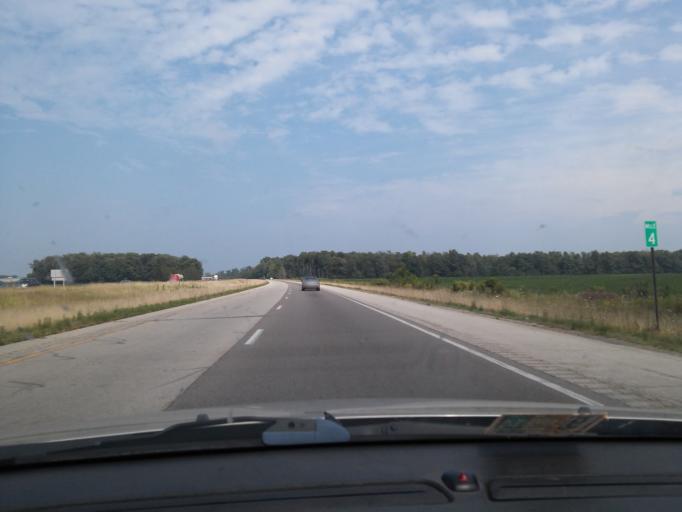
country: US
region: Ohio
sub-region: Preble County
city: New Paris
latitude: 39.8288
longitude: -84.7393
